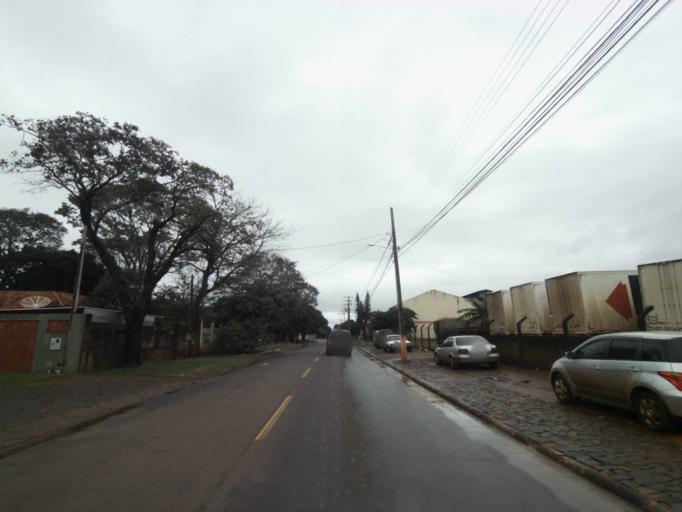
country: BR
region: Parana
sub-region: Foz Do Iguacu
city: Foz do Iguacu
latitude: -25.5122
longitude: -54.5606
